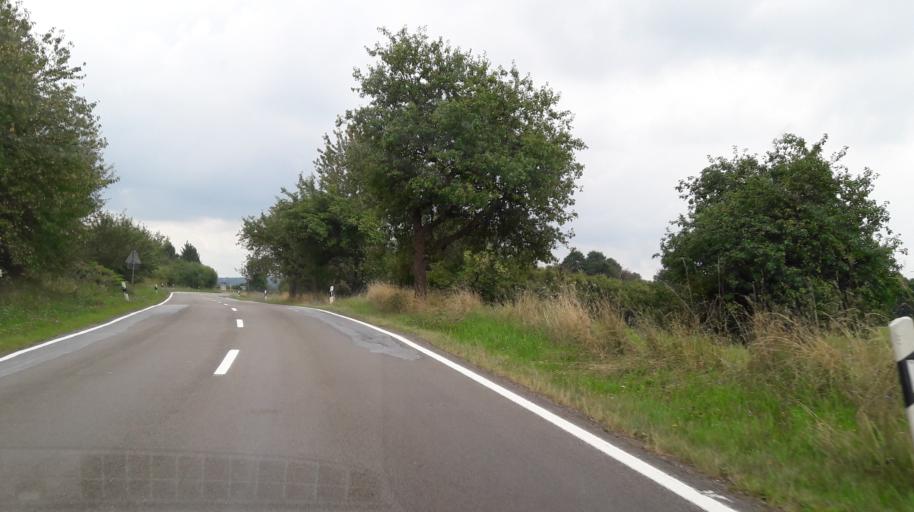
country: DE
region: Saarland
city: Oberthal
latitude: 49.4820
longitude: 7.1149
